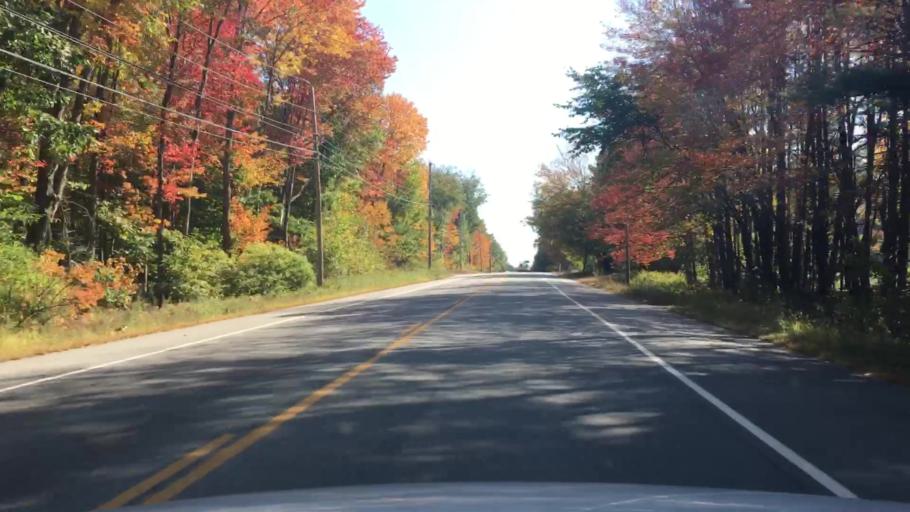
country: US
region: Maine
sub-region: Androscoggin County
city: Lisbon Falls
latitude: 43.9689
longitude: -70.0210
